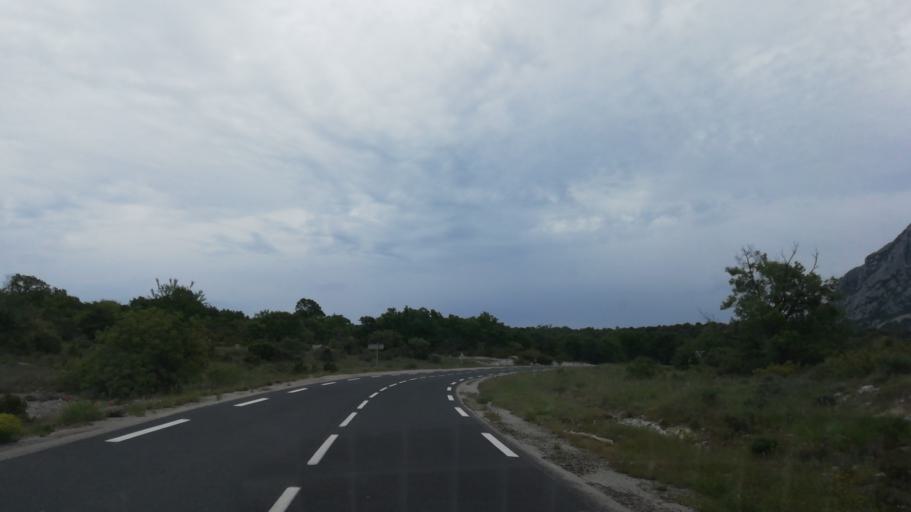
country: FR
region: Languedoc-Roussillon
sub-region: Departement de l'Herault
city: Saint-Mathieu-de-Treviers
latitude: 43.7936
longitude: 3.8014
